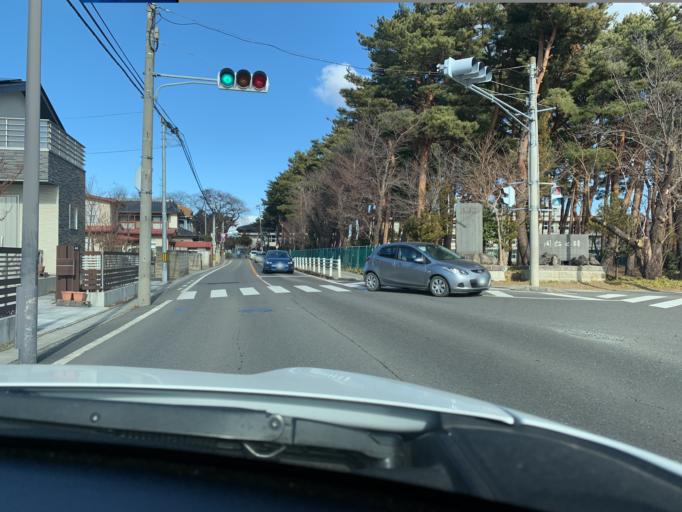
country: JP
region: Fukushima
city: Koriyama
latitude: 37.3949
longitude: 140.3194
